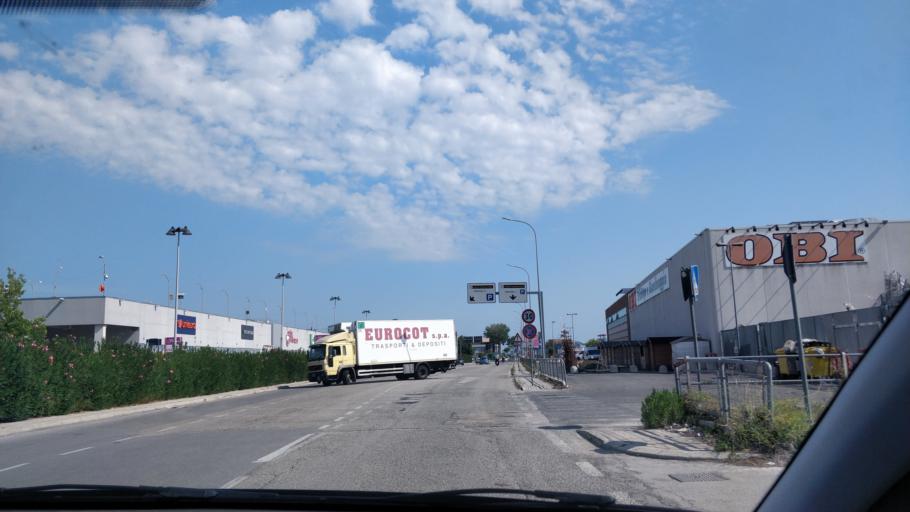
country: IT
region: Abruzzo
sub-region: Provincia di Pescara
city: Santa Teresa
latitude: 42.4139
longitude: 14.1692
